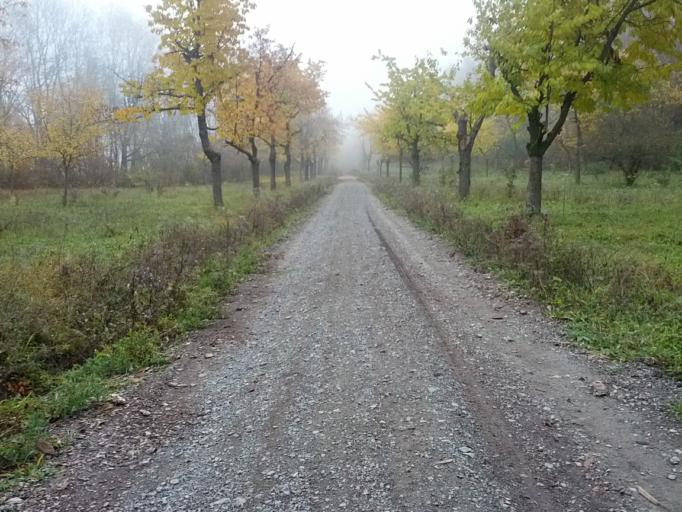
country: DE
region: Thuringia
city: Eisenach
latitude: 50.9710
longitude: 10.3609
